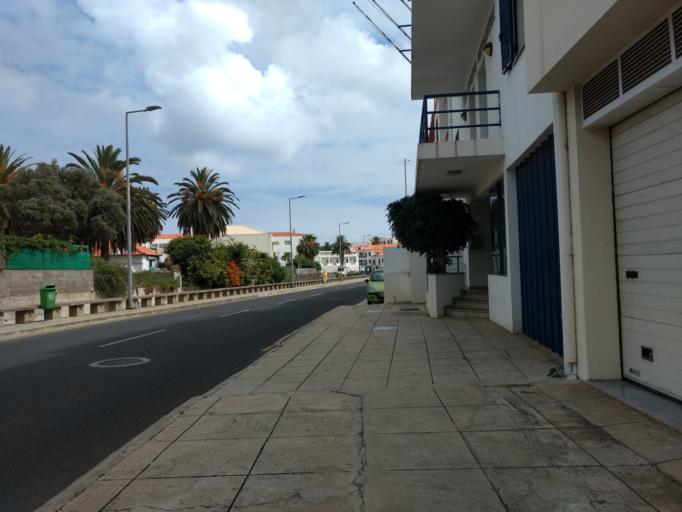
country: PT
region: Madeira
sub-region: Porto Santo
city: Vila de Porto Santo
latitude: 33.0622
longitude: -16.3350
